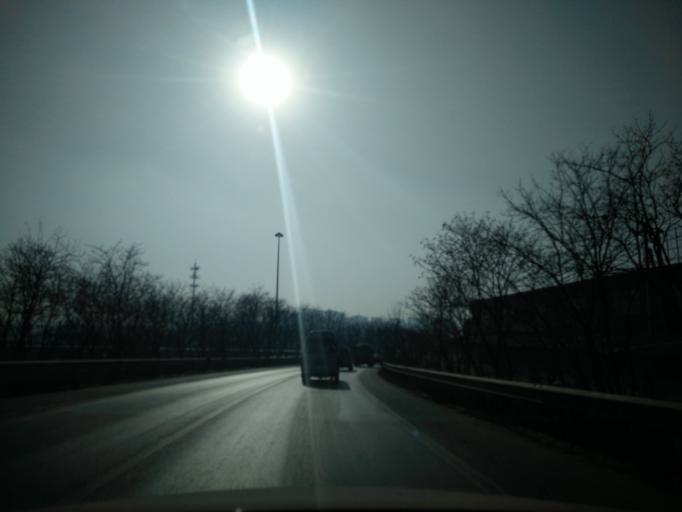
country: CN
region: Beijing
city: Jiugong
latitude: 39.8188
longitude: 116.4957
